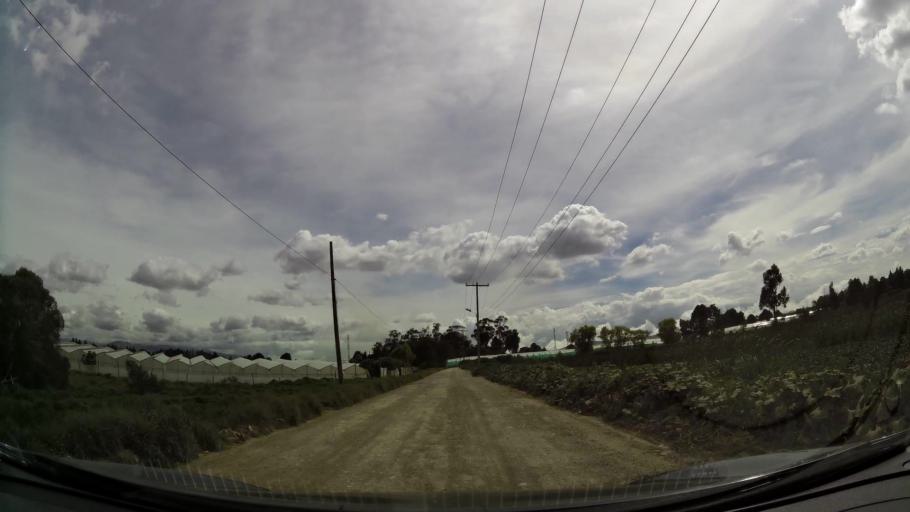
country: CO
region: Cundinamarca
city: Funza
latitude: 4.7054
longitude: -74.1796
